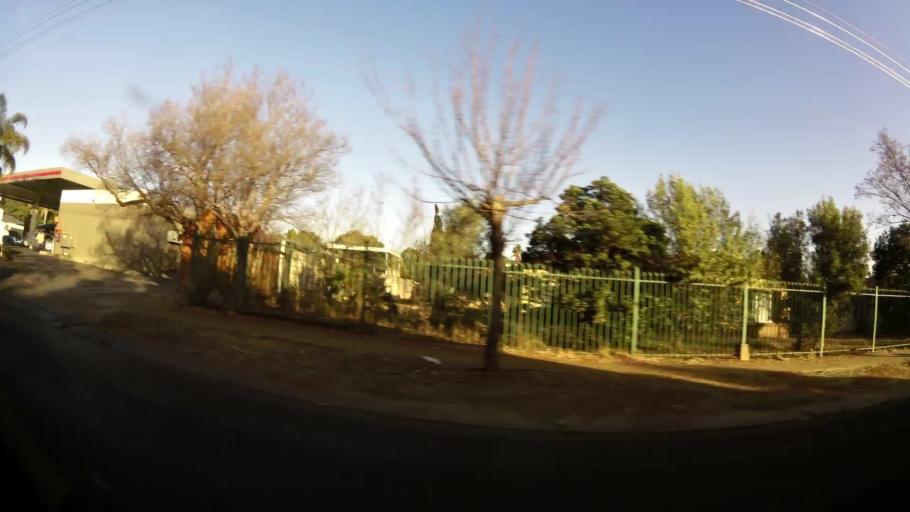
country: ZA
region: Gauteng
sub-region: City of Tshwane Metropolitan Municipality
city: Pretoria
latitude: -25.7048
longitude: 28.2252
